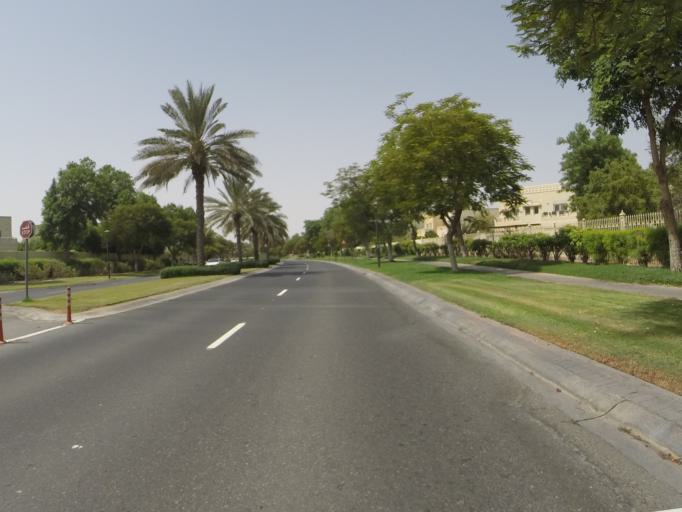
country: AE
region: Dubai
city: Dubai
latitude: 25.0696
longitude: 55.1553
